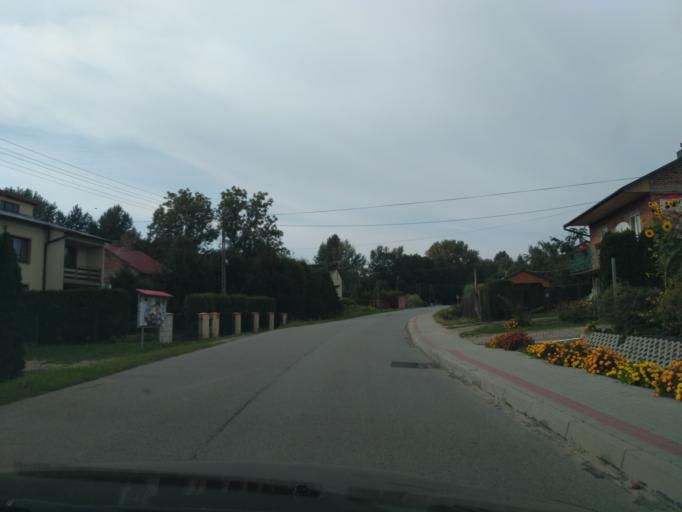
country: PL
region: Subcarpathian Voivodeship
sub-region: Powiat rzeszowski
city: Zglobien
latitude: 50.0383
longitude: 21.8374
